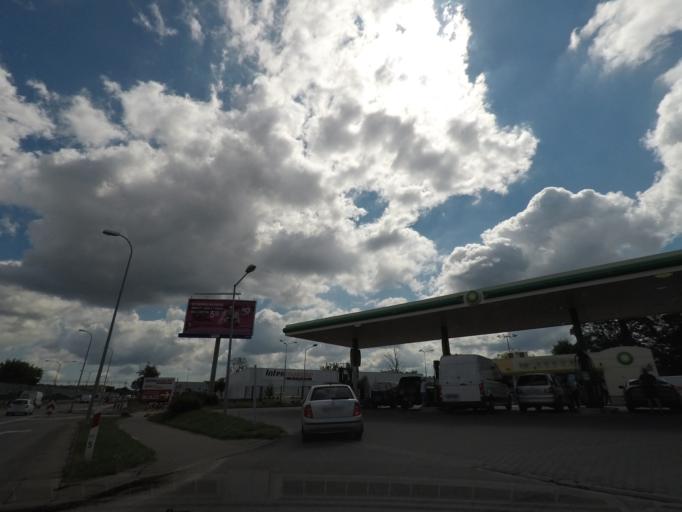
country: PL
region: Pomeranian Voivodeship
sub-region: Powiat wejherowski
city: Wejherowo
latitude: 54.6074
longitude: 18.2248
